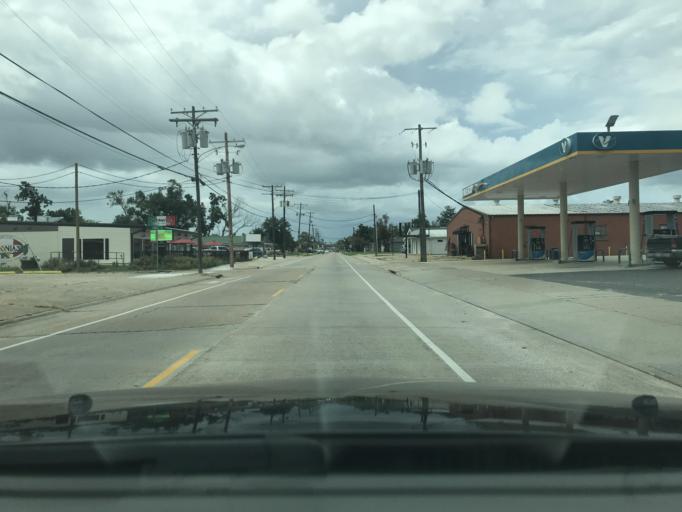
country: US
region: Louisiana
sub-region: Calcasieu Parish
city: Lake Charles
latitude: 30.2014
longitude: -93.2099
